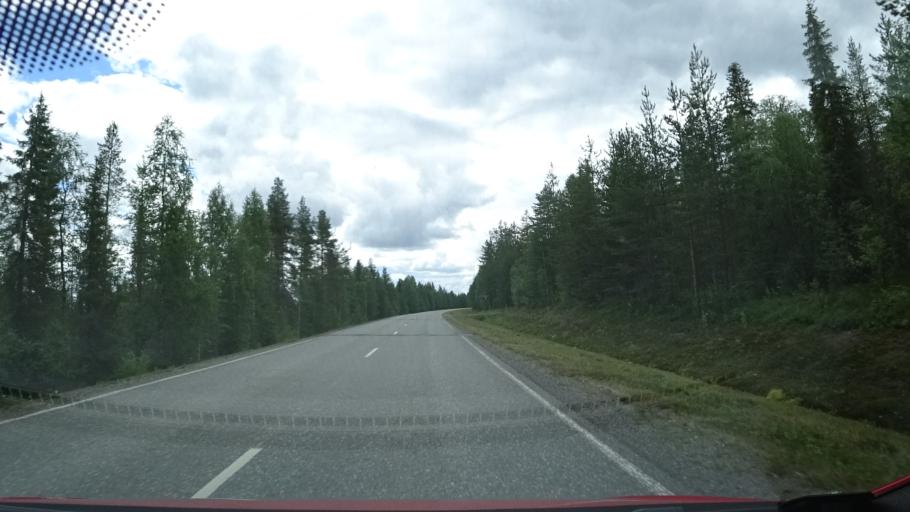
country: FI
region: Lapland
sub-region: Tunturi-Lappi
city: Kittilae
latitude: 67.6096
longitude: 24.9408
